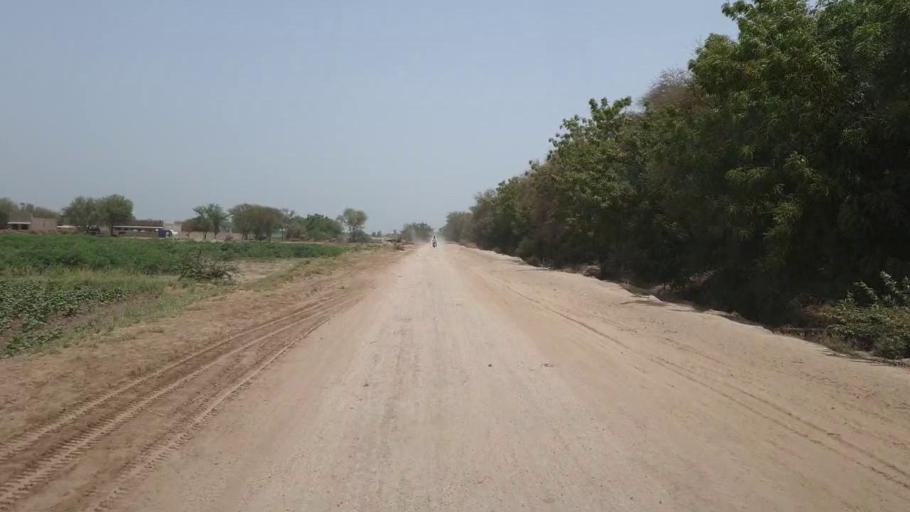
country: PK
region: Sindh
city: Nawabshah
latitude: 26.3209
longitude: 68.2978
